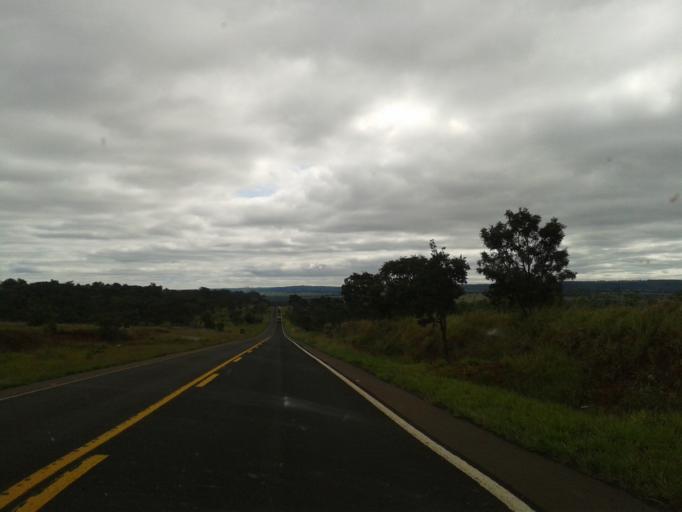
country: BR
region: Minas Gerais
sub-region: Campina Verde
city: Campina Verde
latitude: -19.5213
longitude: -49.6326
